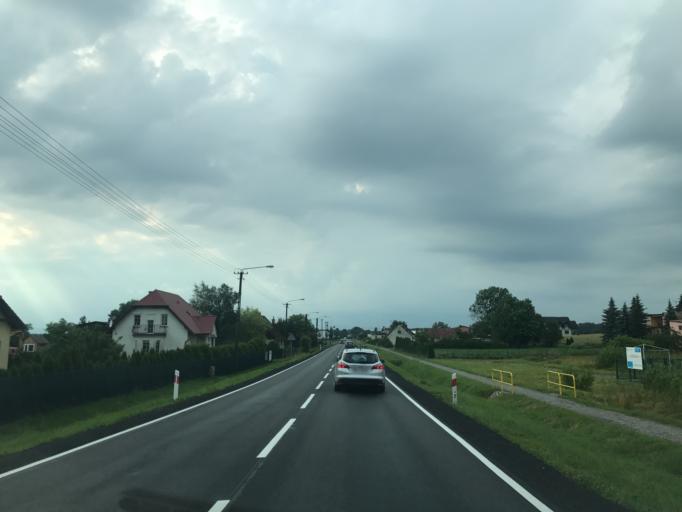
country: PL
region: Pomeranian Voivodeship
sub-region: Powiat czluchowski
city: Czluchow
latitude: 53.6801
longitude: 17.3380
